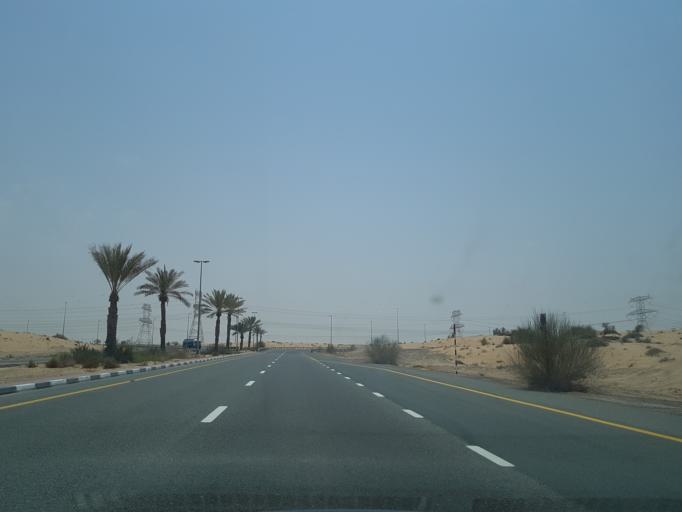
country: AE
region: Ash Shariqah
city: Sharjah
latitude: 25.1053
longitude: 55.4127
